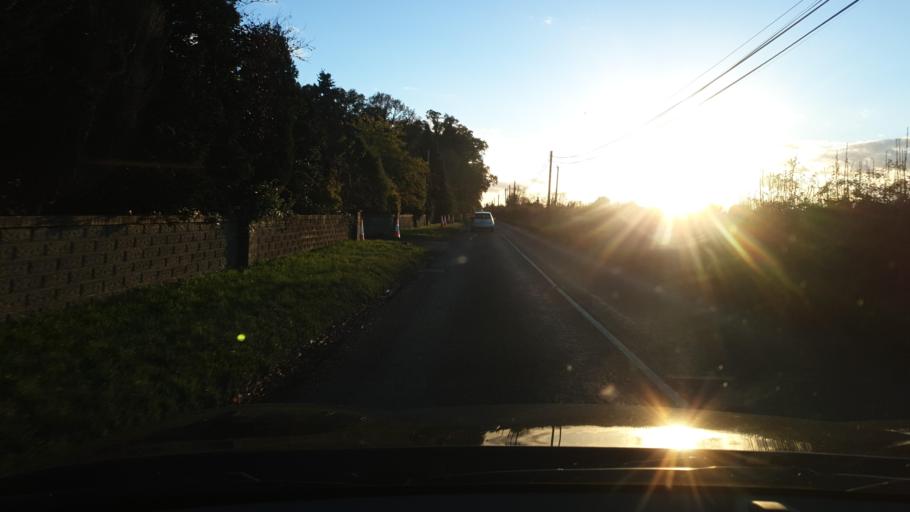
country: IE
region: Leinster
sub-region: Lu
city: Drogheda
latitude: 53.7377
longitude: -6.3081
